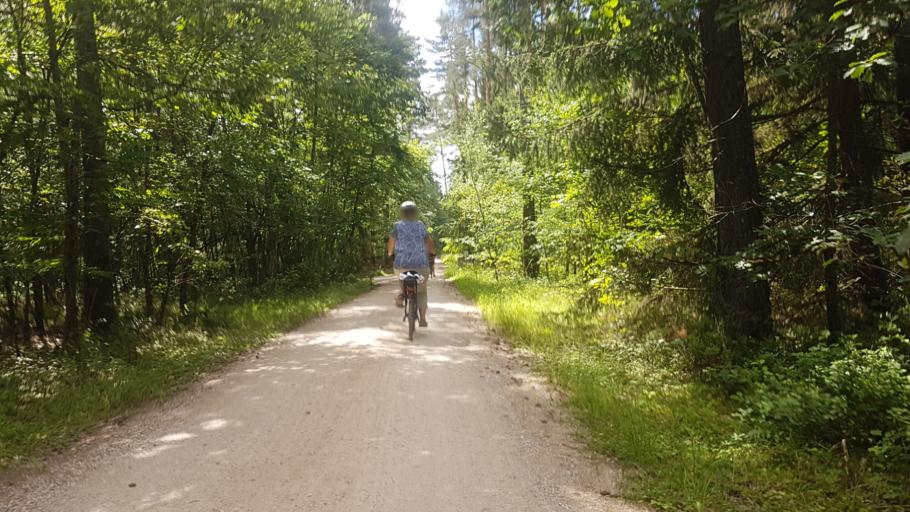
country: DE
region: Bavaria
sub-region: Regierungsbezirk Mittelfranken
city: Pfofeld
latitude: 49.1255
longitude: 10.8229
